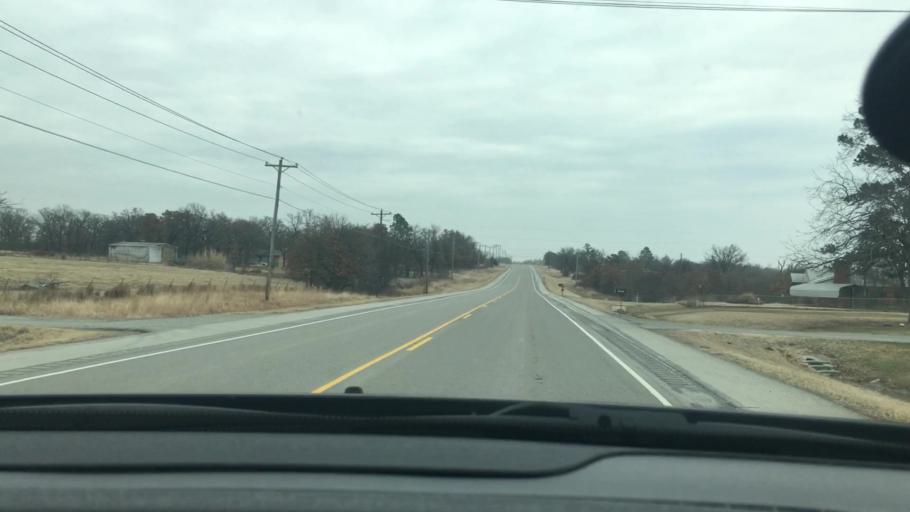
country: US
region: Oklahoma
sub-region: Carter County
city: Healdton
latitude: 34.4026
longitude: -97.5074
